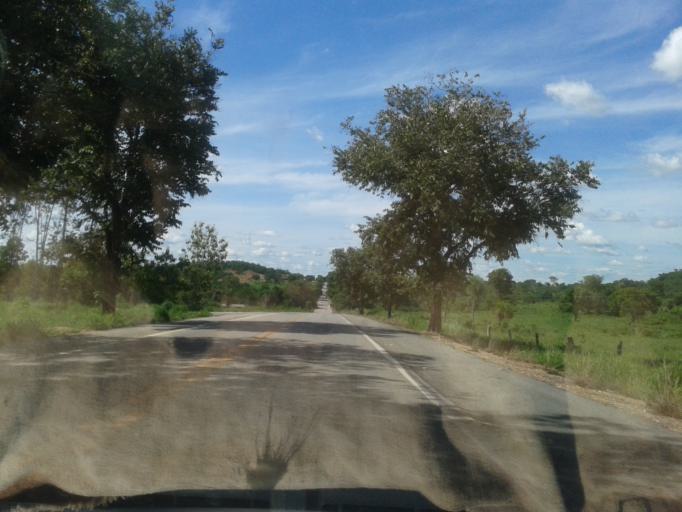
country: BR
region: Goias
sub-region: Itapuranga
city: Itapuranga
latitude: -15.4333
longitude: -50.3715
